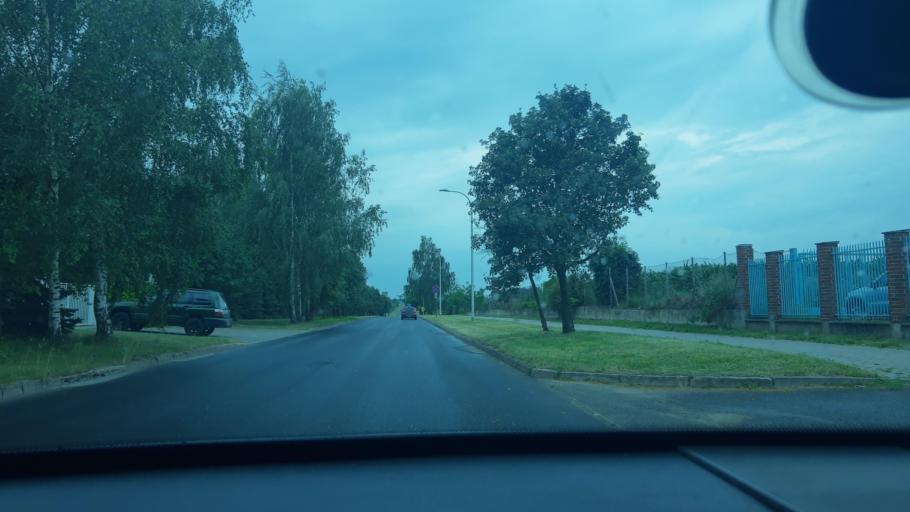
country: PL
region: Lodz Voivodeship
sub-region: Powiat sieradzki
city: Sieradz
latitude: 51.5807
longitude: 18.7071
